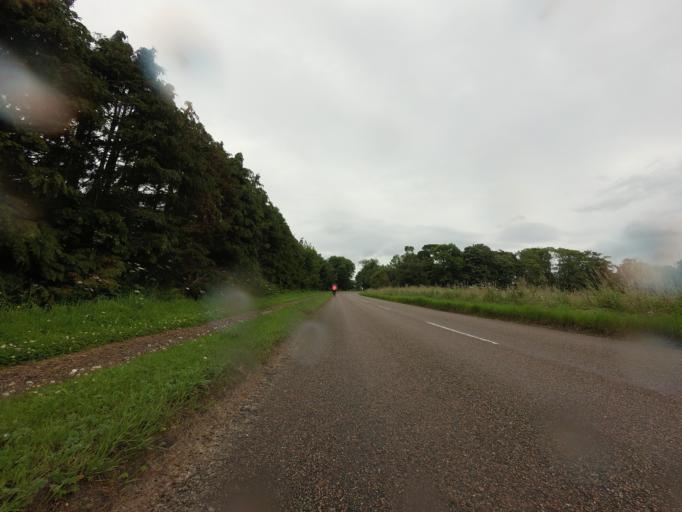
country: GB
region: Scotland
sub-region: Moray
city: Cullen
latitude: 57.6826
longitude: -2.8142
